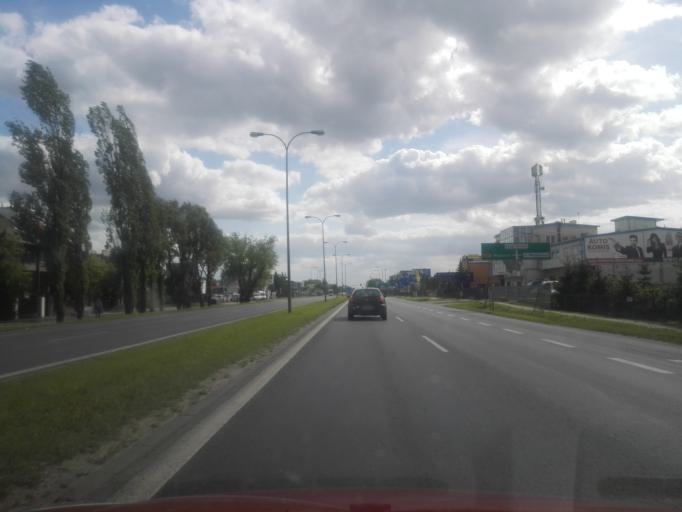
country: PL
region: Masovian Voivodeship
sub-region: Powiat wolominski
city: Zabki
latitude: 52.2899
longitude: 21.0777
